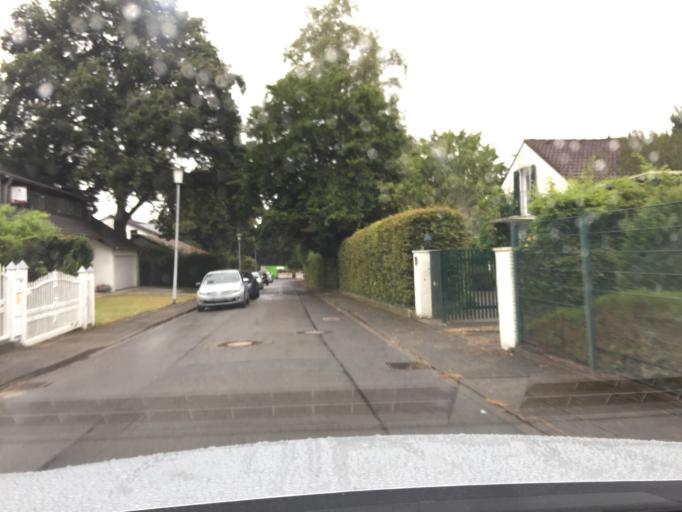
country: DE
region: North Rhine-Westphalia
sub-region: Regierungsbezirk Dusseldorf
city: Ratingen
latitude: 51.3365
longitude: 6.8973
